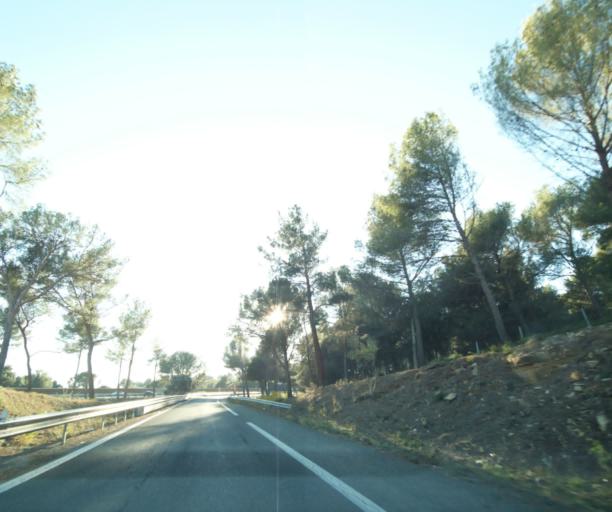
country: FR
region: Provence-Alpes-Cote d'Azur
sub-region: Departement du Var
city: Saint-Cyr-sur-Mer
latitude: 43.1945
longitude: 5.6877
